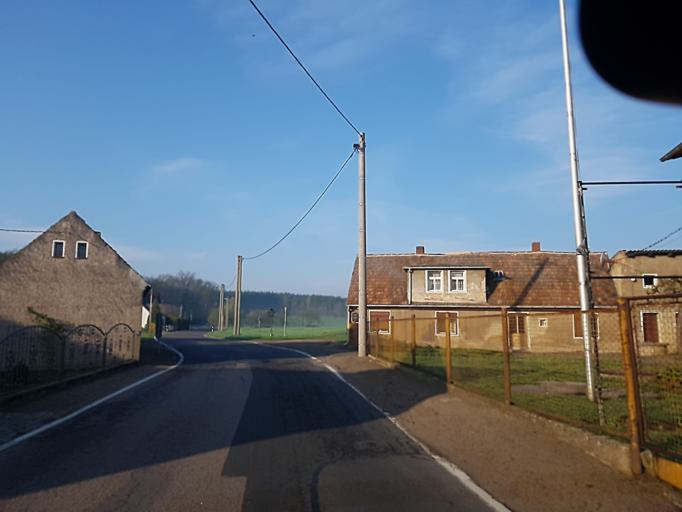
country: DE
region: Saxony
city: Cavertitz
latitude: 51.4341
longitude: 13.1589
